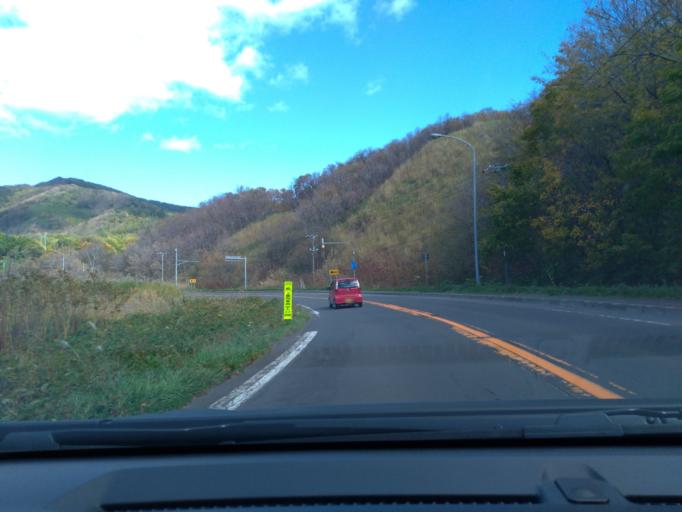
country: JP
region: Hokkaido
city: Ishikari
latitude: 43.4125
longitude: 141.4323
